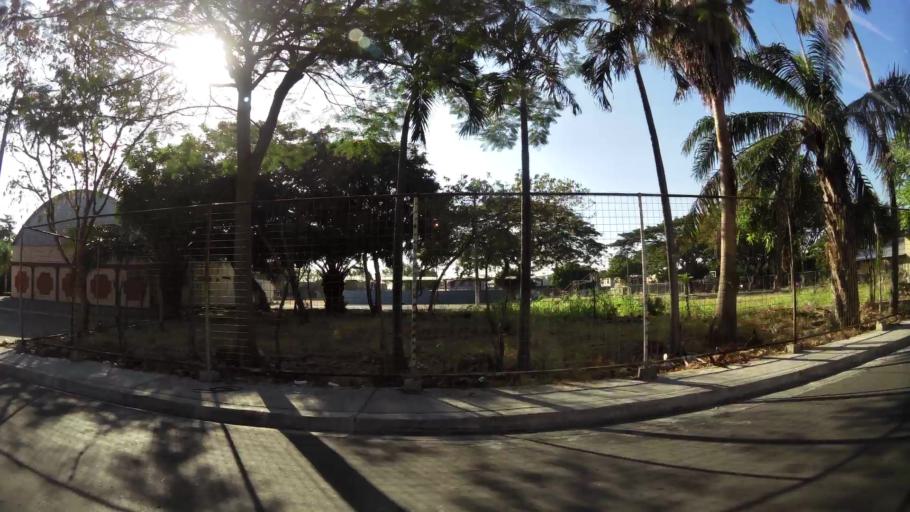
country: EC
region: Guayas
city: Eloy Alfaro
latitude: -2.1683
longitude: -79.8870
